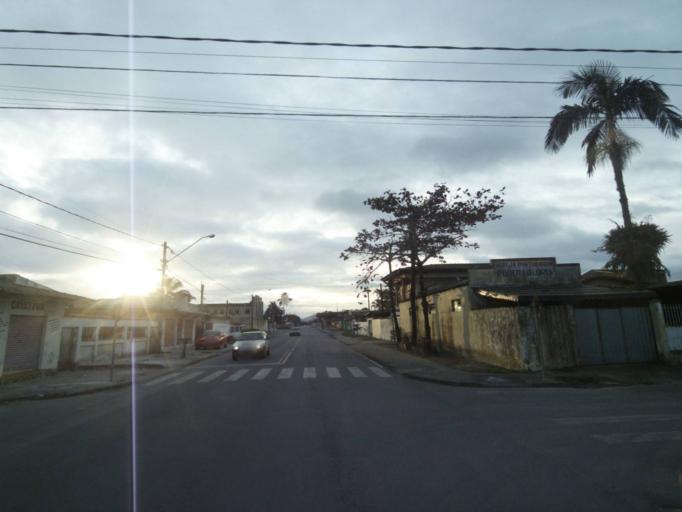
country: BR
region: Parana
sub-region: Paranagua
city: Paranagua
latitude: -25.5175
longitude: -48.5415
